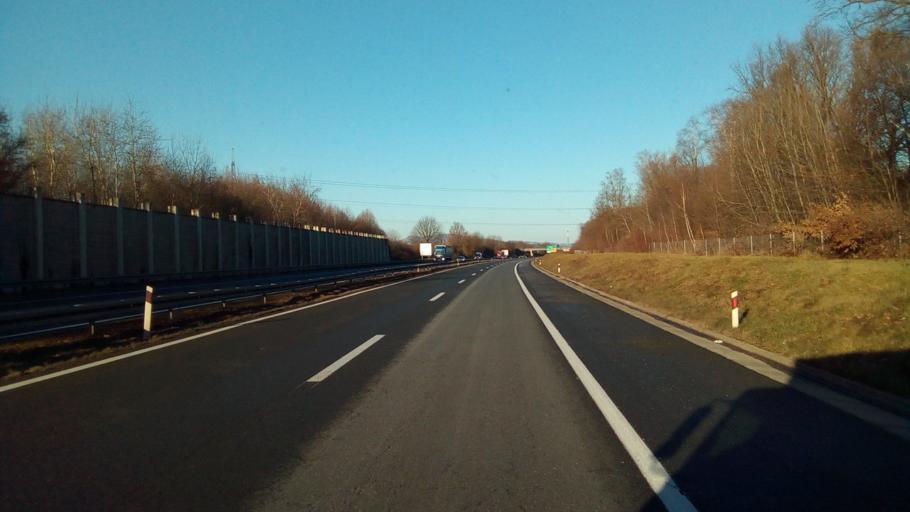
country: HR
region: Zagrebacka
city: Kerestinec
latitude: 45.7884
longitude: 15.8004
